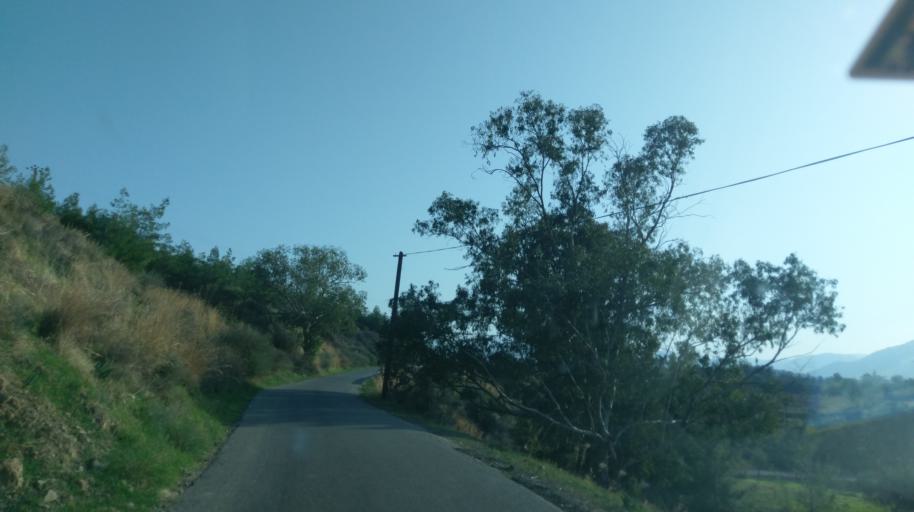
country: CY
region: Lefkosia
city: Lefka
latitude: 35.1138
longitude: 32.8601
